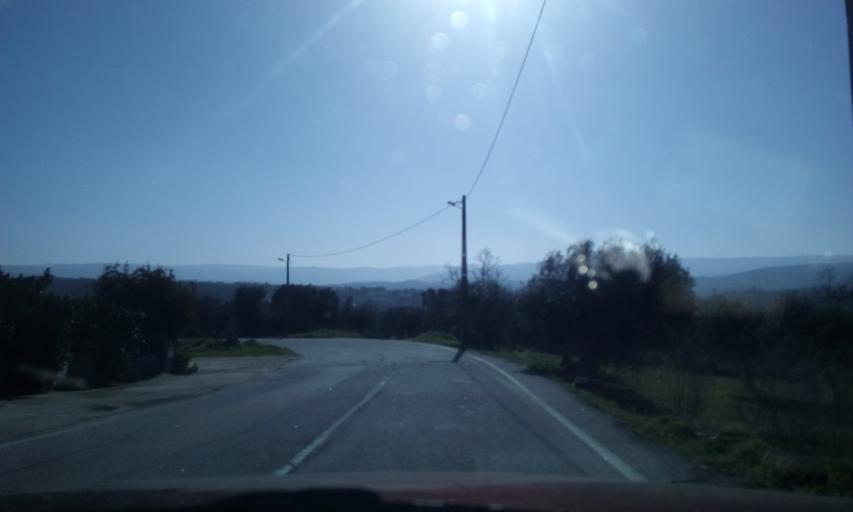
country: PT
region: Guarda
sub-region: Celorico da Beira
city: Celorico da Beira
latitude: 40.6713
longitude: -7.3943
